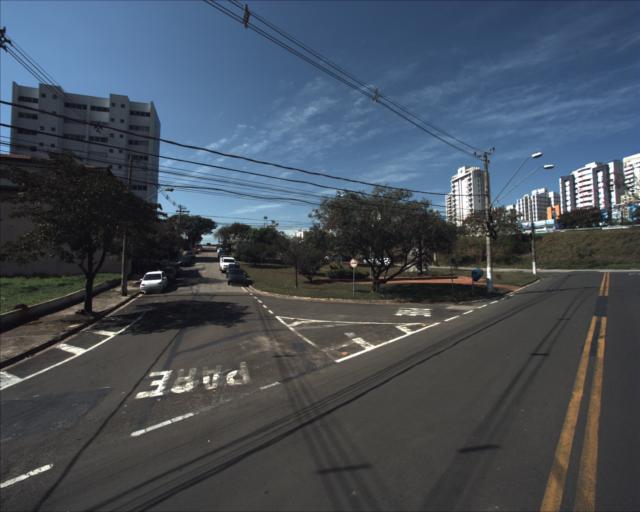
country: BR
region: Sao Paulo
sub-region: Sorocaba
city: Sorocaba
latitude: -23.5293
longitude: -47.4685
